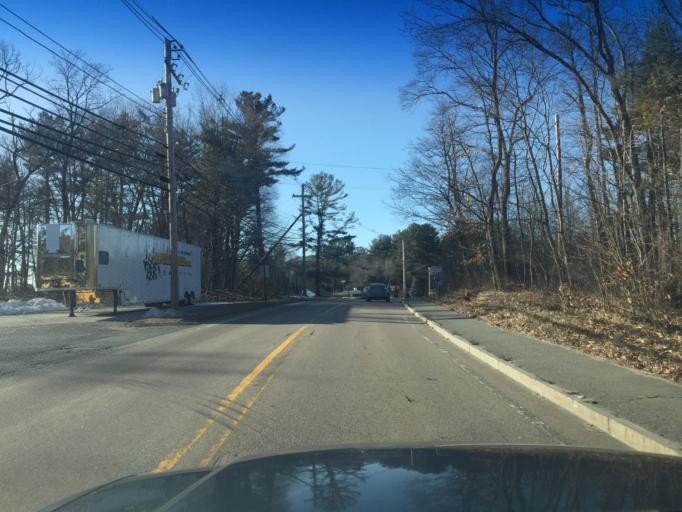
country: US
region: Massachusetts
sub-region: Norfolk County
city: Bellingham
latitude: 42.0882
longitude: -71.4976
